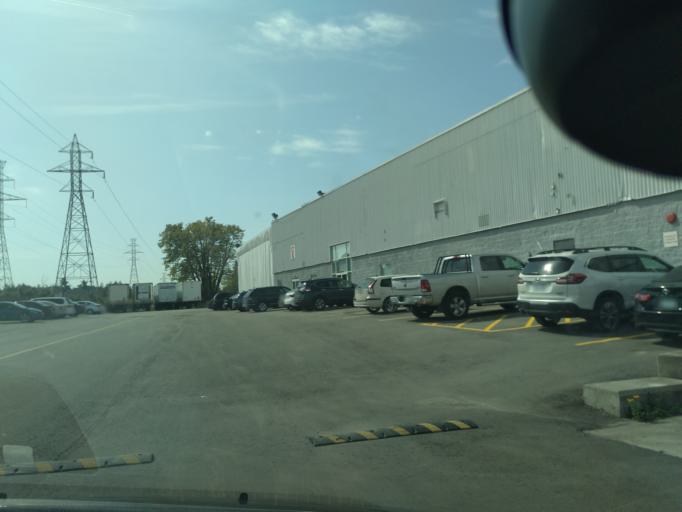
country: CA
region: Ontario
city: Newmarket
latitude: 44.0374
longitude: -79.4571
